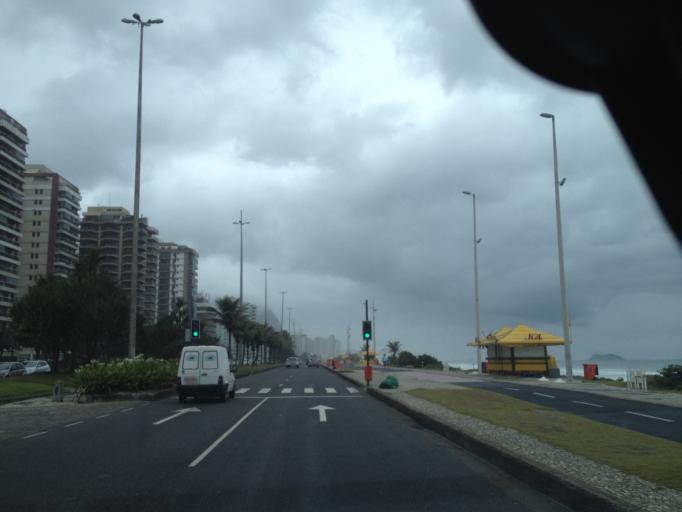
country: BR
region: Rio de Janeiro
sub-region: Rio De Janeiro
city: Rio de Janeiro
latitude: -23.0106
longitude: -43.3579
